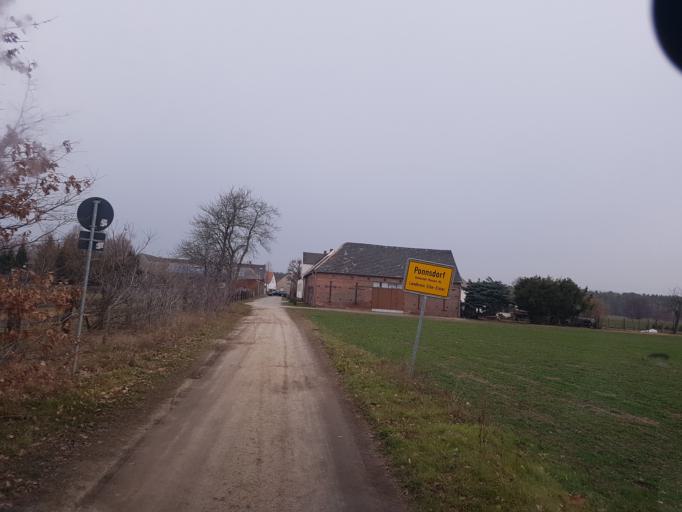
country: DE
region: Brandenburg
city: Finsterwalde
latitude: 51.6621
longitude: 13.6864
